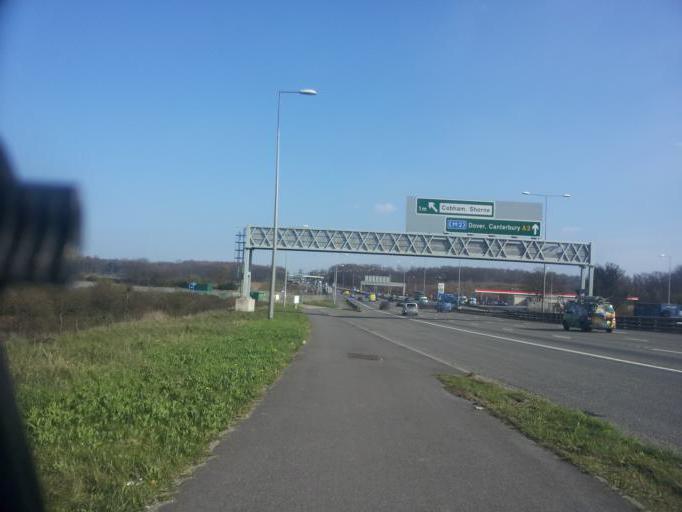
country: GB
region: England
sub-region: Kent
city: Gravesend
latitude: 51.4064
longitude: 0.3931
